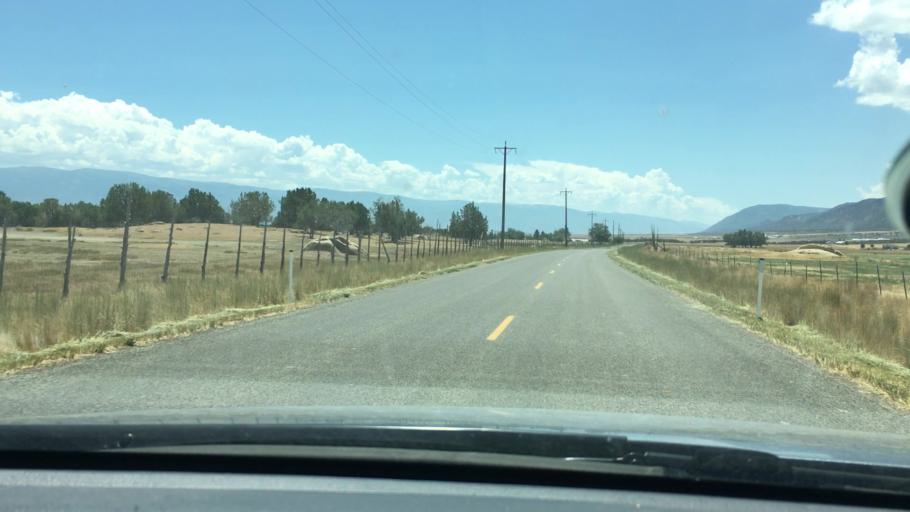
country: US
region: Utah
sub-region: Sanpete County
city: Fountain Green
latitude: 39.6079
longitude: -111.6440
